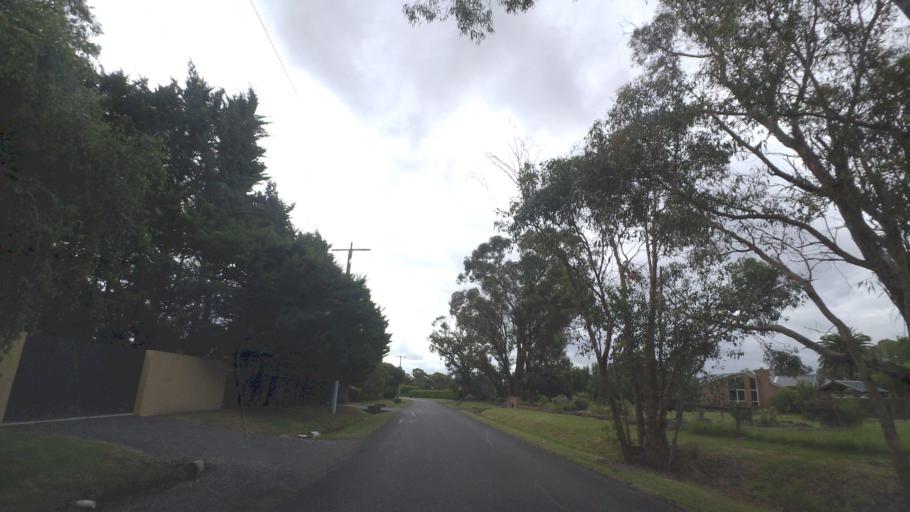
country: AU
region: Victoria
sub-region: Maroondah
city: Kilsyth South
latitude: -37.8252
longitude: 145.3169
